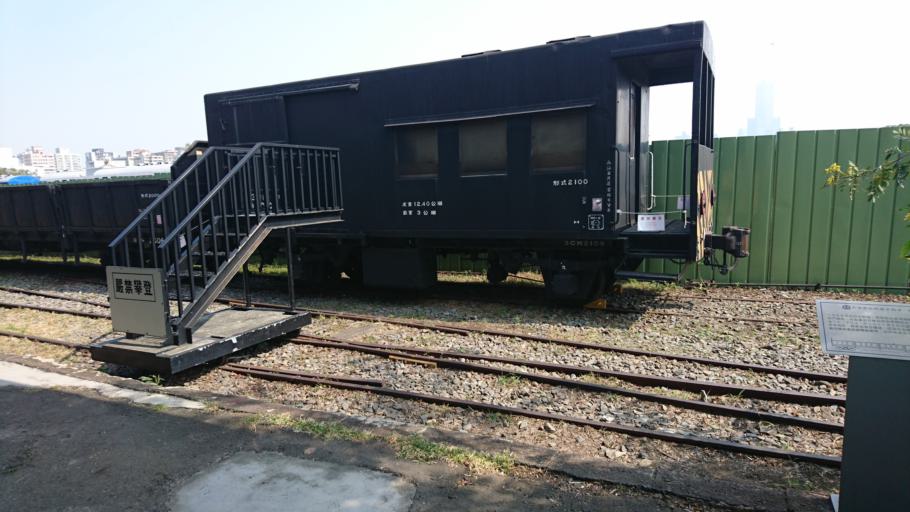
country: TW
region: Kaohsiung
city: Kaohsiung
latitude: 22.6215
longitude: 120.2756
